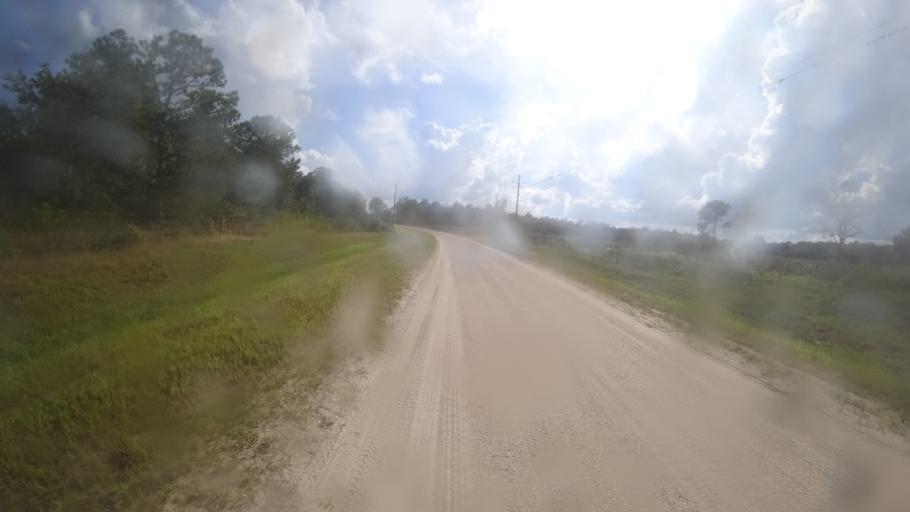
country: US
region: Florida
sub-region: Hillsborough County
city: Wimauma
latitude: 27.5944
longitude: -82.1225
